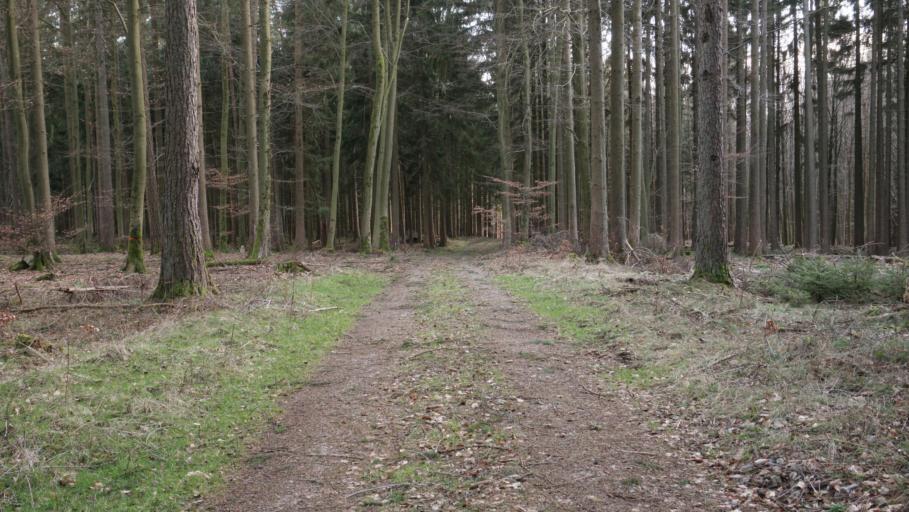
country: DE
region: Baden-Wuerttemberg
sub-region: Karlsruhe Region
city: Fahrenbach
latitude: 49.4457
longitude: 9.1190
